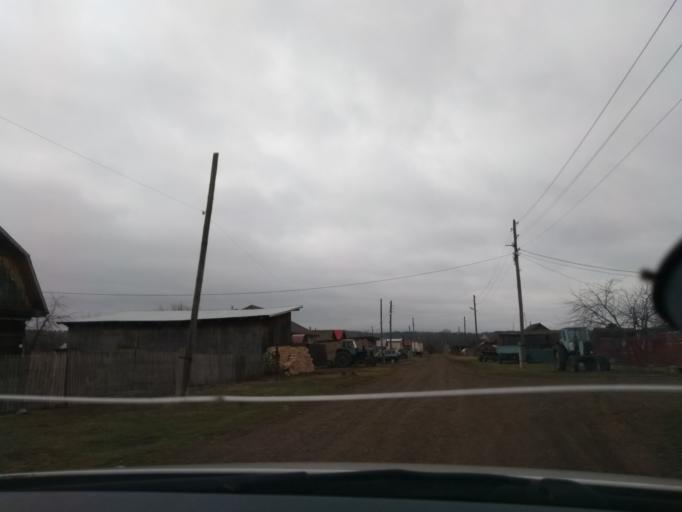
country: RU
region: Perm
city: Orda
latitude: 57.2153
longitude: 56.6009
